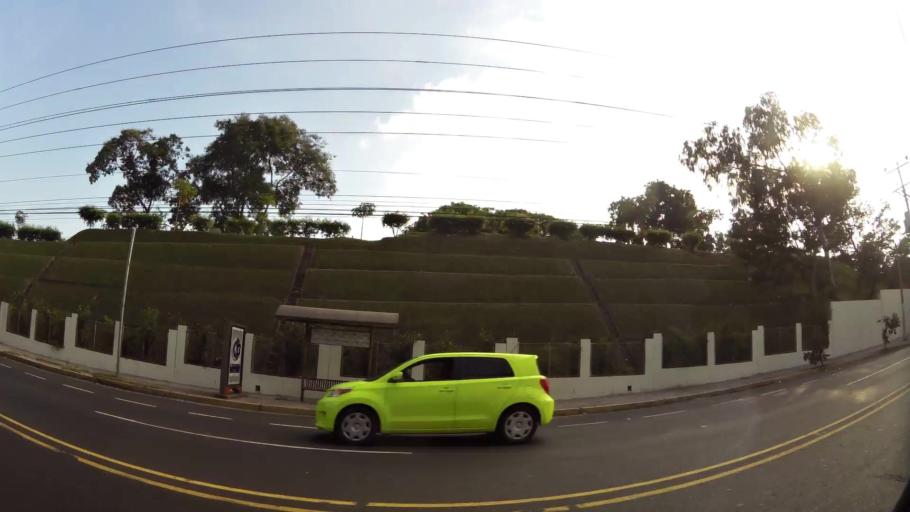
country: SV
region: San Salvador
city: San Salvador
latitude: 13.6918
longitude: -89.2111
